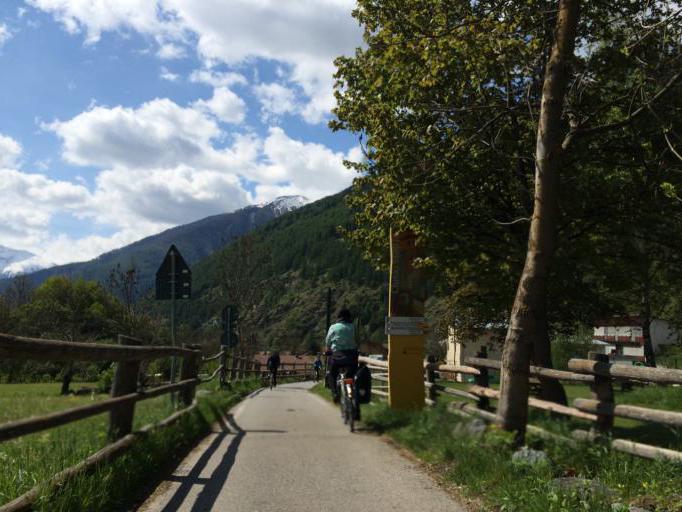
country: IT
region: Trentino-Alto Adige
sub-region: Bolzano
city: Malles Venosta
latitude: 46.6965
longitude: 10.5226
